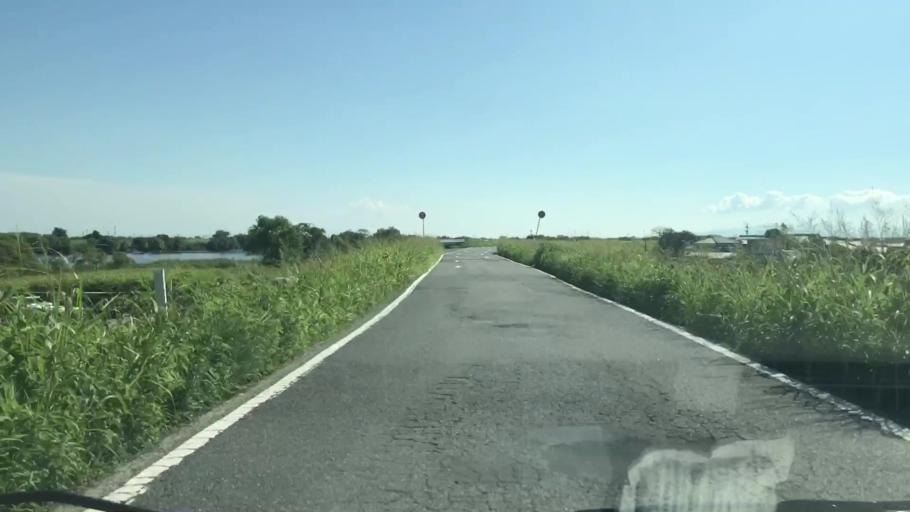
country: JP
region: Fukuoka
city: Kurume
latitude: 33.2809
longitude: 130.4481
